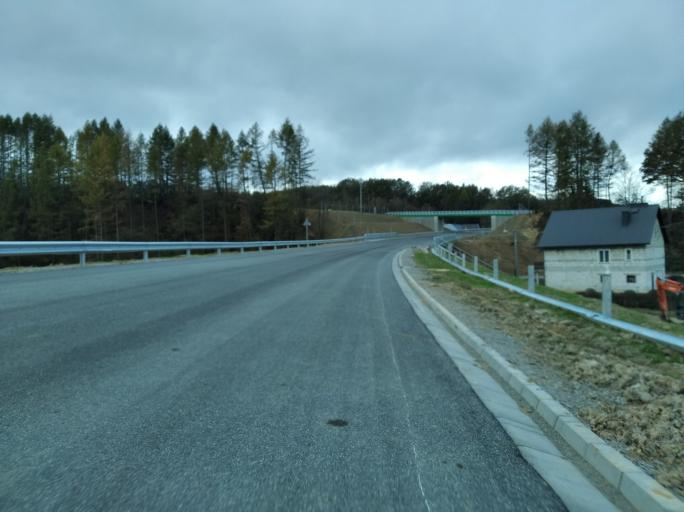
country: PL
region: Subcarpathian Voivodeship
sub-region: Powiat strzyzowski
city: Strzyzow
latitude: 49.8618
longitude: 21.8143
